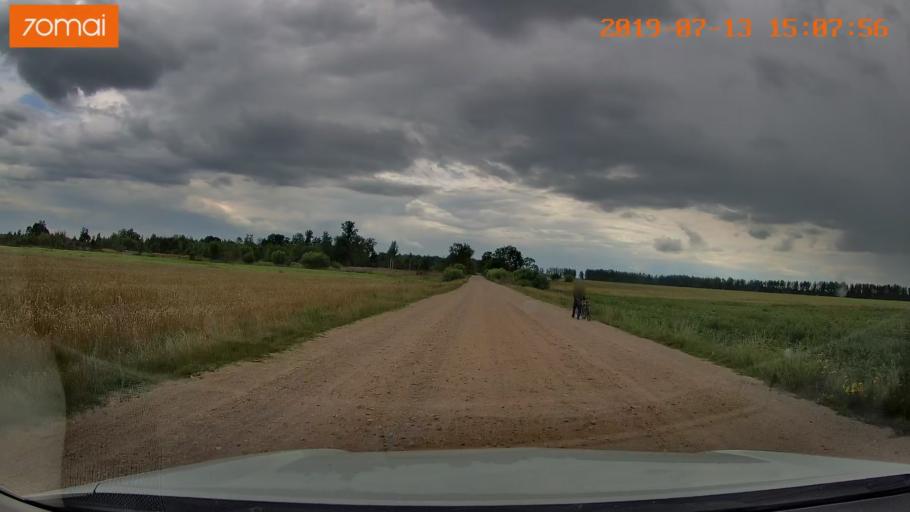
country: BY
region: Mogilev
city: Hlusha
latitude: 53.1847
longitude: 28.7573
